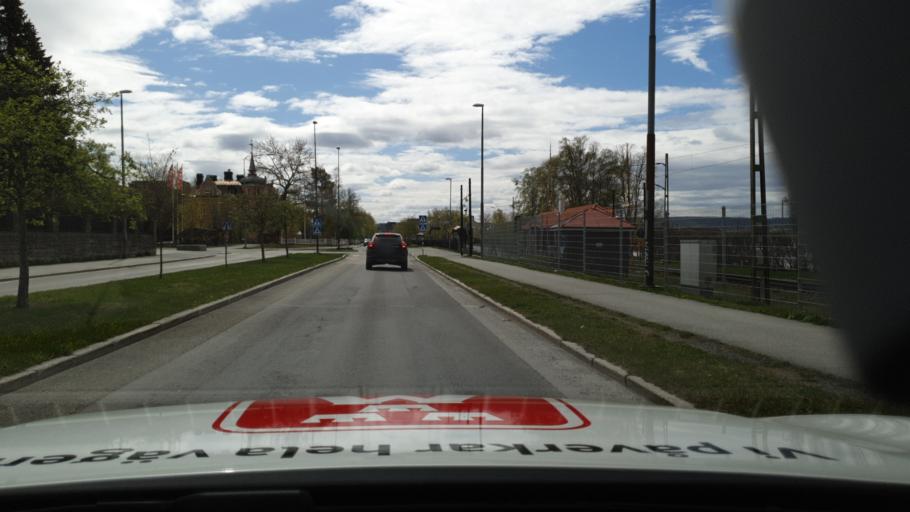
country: SE
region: Jaemtland
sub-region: OEstersunds Kommun
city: Ostersund
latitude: 63.1797
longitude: 14.6313
